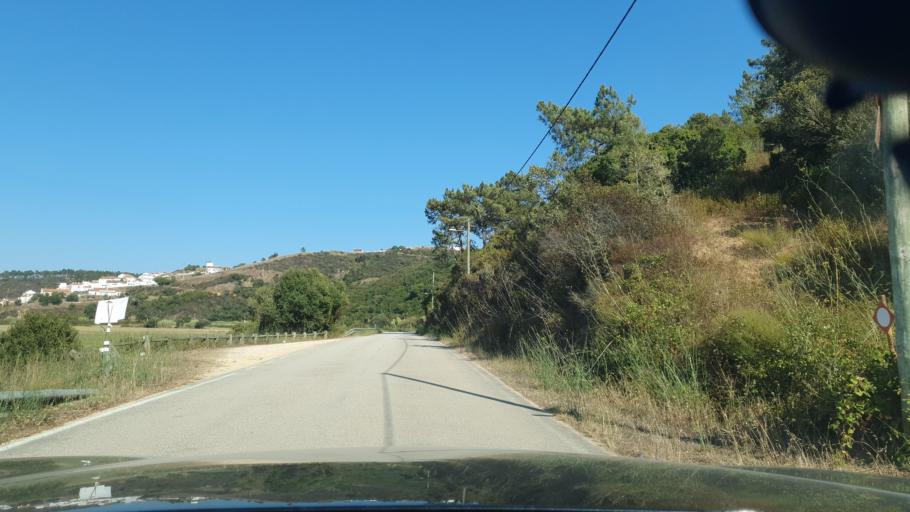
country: PT
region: Beja
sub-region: Odemira
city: Sao Teotonio
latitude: 37.4323
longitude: -8.7809
